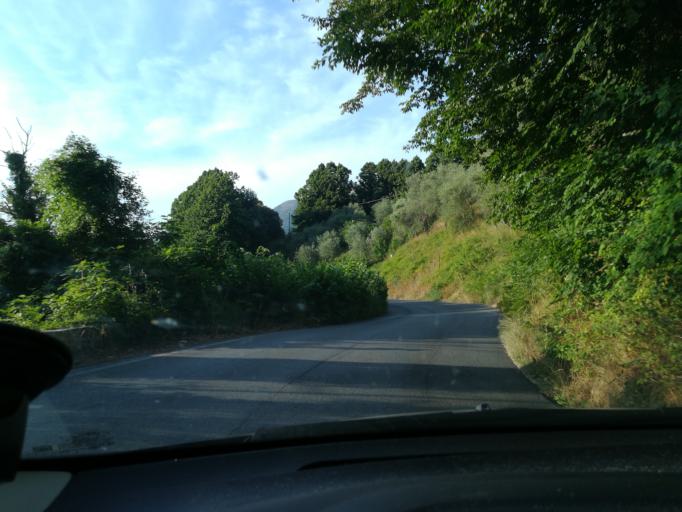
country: IT
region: Tuscany
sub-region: Provincia di Lucca
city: Stiava
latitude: 43.9159
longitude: 10.3390
